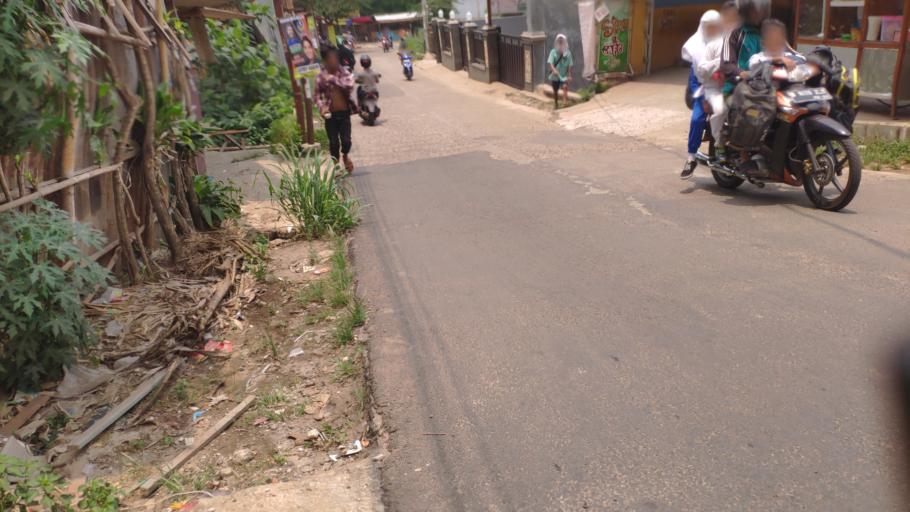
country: ID
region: West Java
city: Sawangan
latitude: -6.3840
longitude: 106.7872
